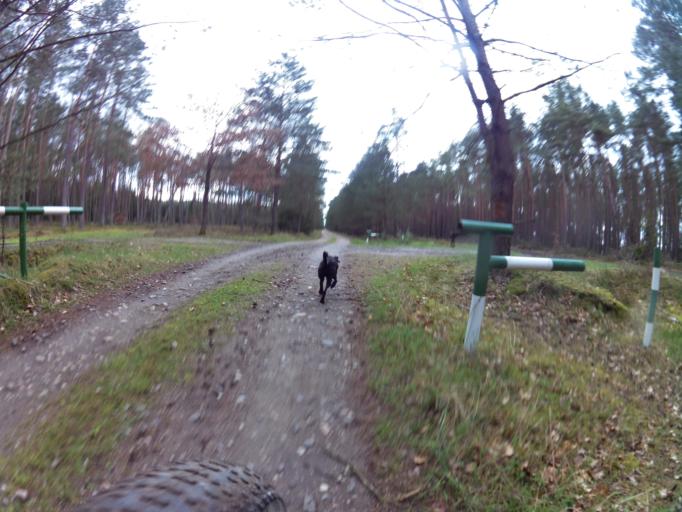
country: PL
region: Pomeranian Voivodeship
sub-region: Powiat slupski
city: Kepice
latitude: 54.3171
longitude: 16.7979
